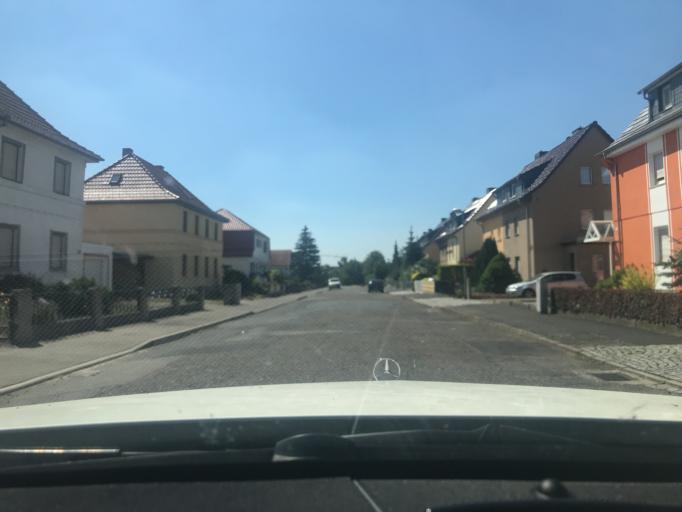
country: DE
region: Thuringia
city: Muehlhausen
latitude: 51.2187
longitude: 10.4671
